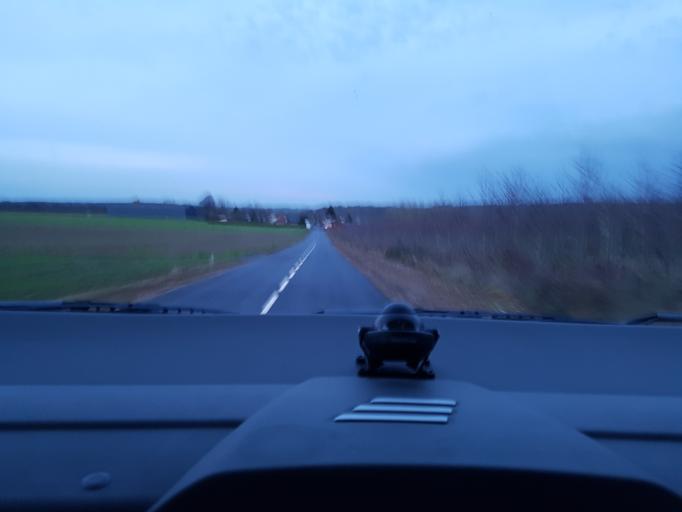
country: FR
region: Picardie
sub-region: Departement de la Somme
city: Beauquesne
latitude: 50.0998
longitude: 2.4364
